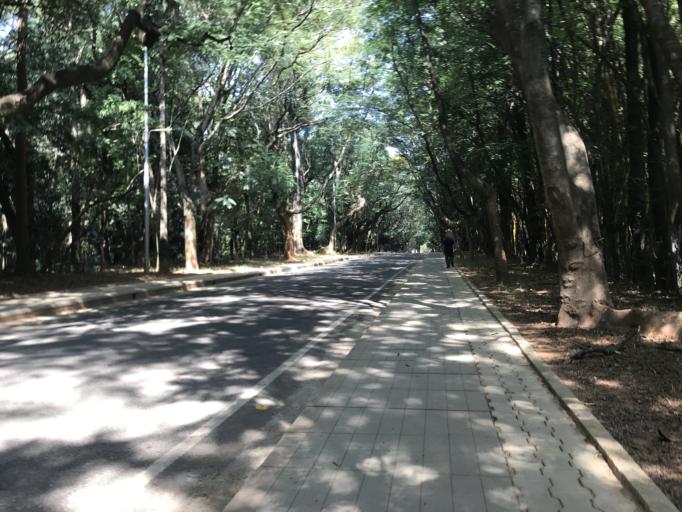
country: IN
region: Karnataka
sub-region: Bangalore Urban
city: Bangalore
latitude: 13.0209
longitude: 77.5664
